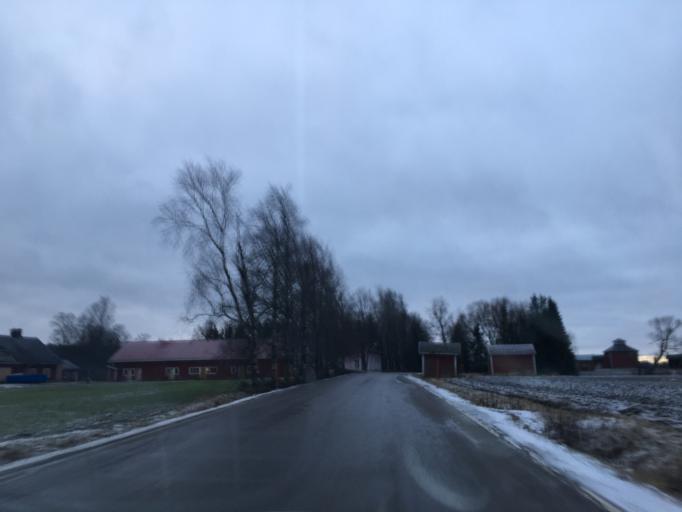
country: FI
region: Varsinais-Suomi
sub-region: Loimaa
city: Aura
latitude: 60.6268
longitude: 22.5838
